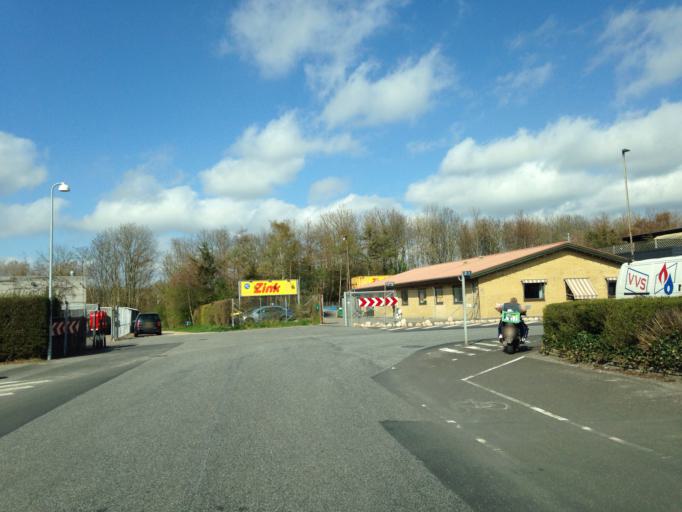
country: DK
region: Zealand
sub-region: Greve Kommune
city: Greve
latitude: 55.5910
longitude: 12.2946
